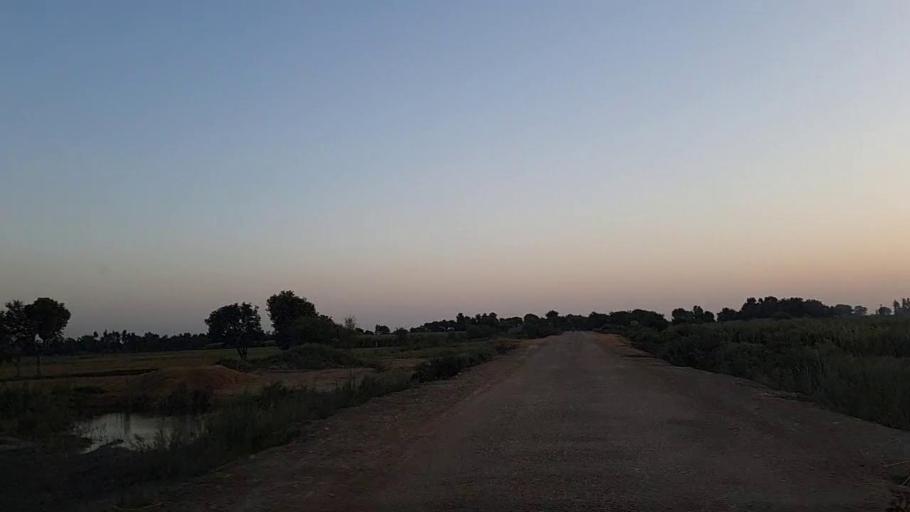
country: PK
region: Sindh
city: Mirpur Batoro
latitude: 24.6204
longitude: 68.1840
